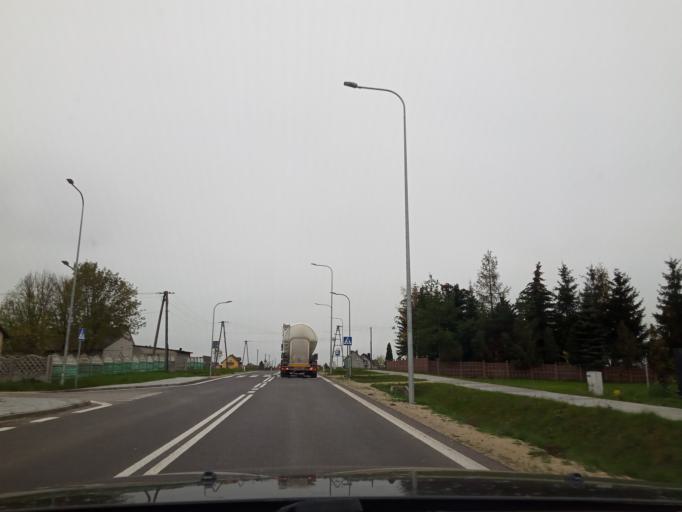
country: PL
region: Swietokrzyskie
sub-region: Powiat jedrzejowski
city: Jedrzejow
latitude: 50.5969
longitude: 20.3216
